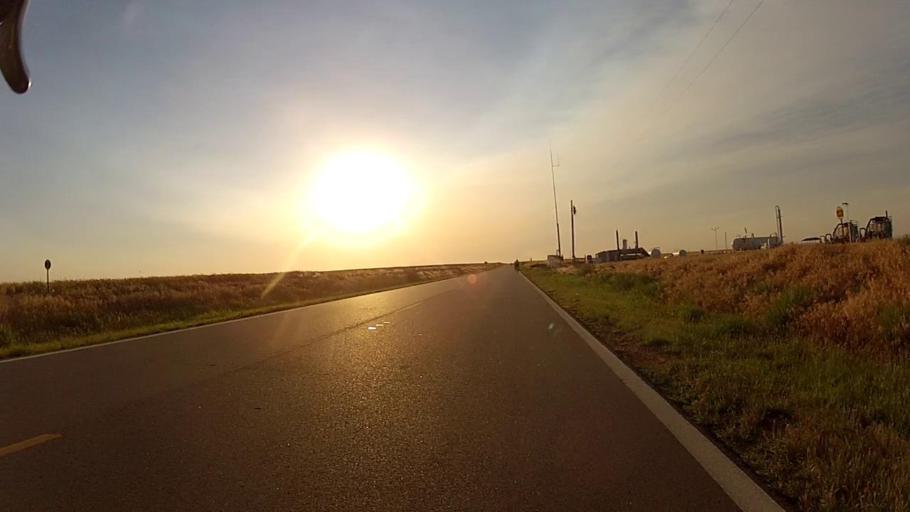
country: US
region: Kansas
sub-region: Harper County
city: Anthony
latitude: 37.1530
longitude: -97.9214
